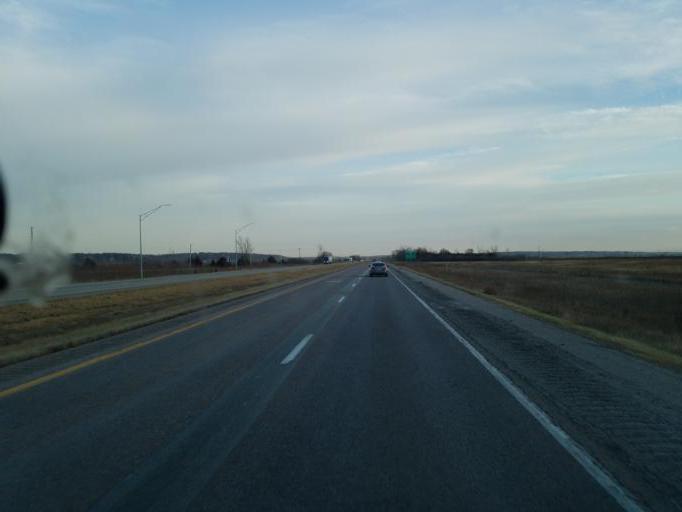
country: US
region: Iowa
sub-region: Harrison County
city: Missouri Valley
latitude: 41.5820
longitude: -95.9402
